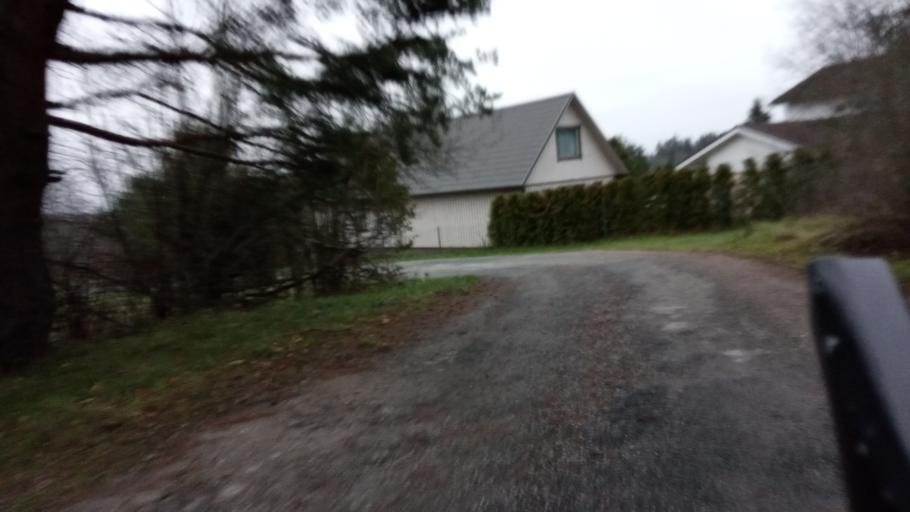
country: EE
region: Harju
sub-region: Kuusalu vald
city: Kuusalu
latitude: 59.4512
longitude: 25.4234
